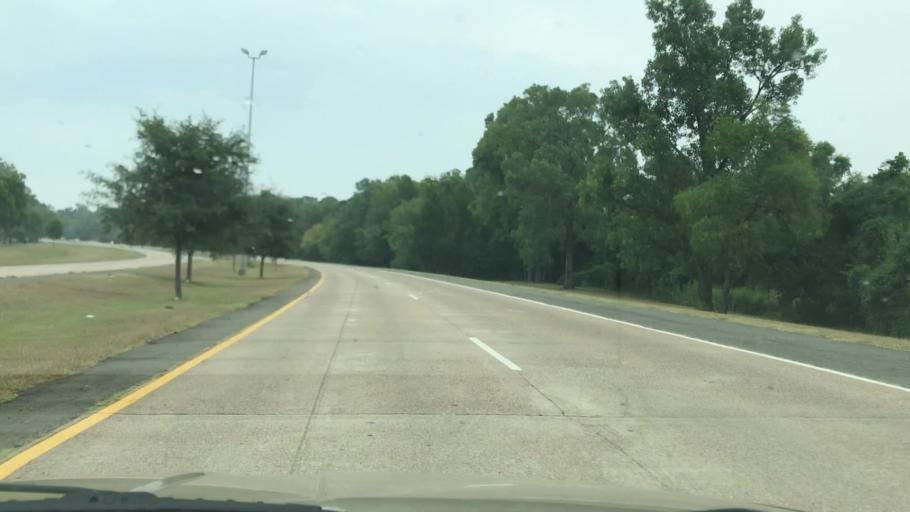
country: US
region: Louisiana
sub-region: Bossier Parish
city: Bossier City
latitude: 32.5081
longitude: -93.7357
